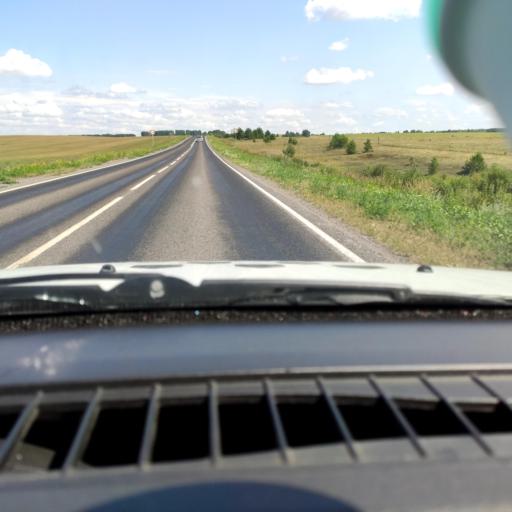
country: RU
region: Bashkortostan
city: Mesyagutovo
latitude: 55.4584
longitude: 58.4231
